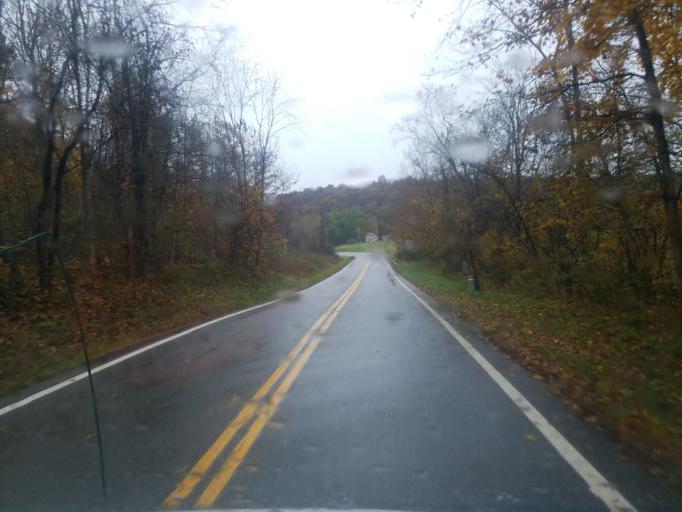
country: US
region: Ohio
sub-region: Washington County
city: Beverly
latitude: 39.4762
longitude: -81.7285
